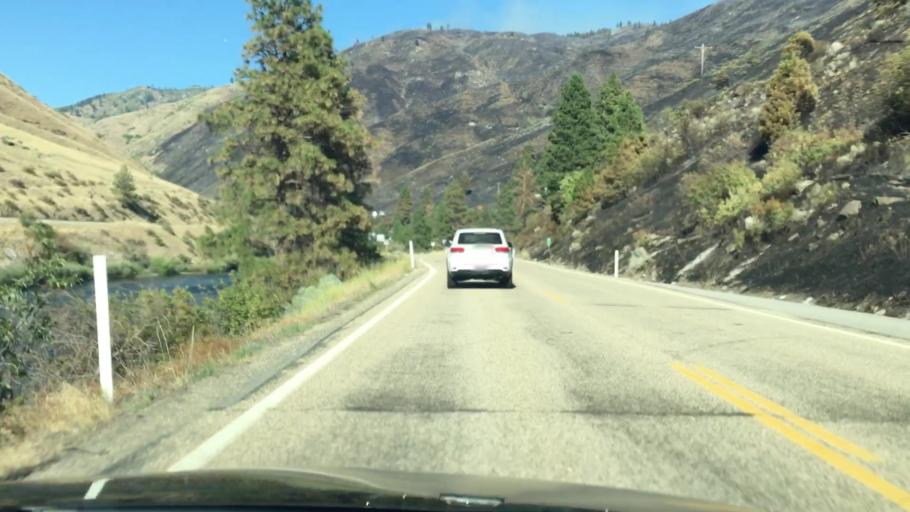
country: US
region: Idaho
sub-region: Gem County
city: Emmett
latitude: 44.0077
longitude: -116.1729
